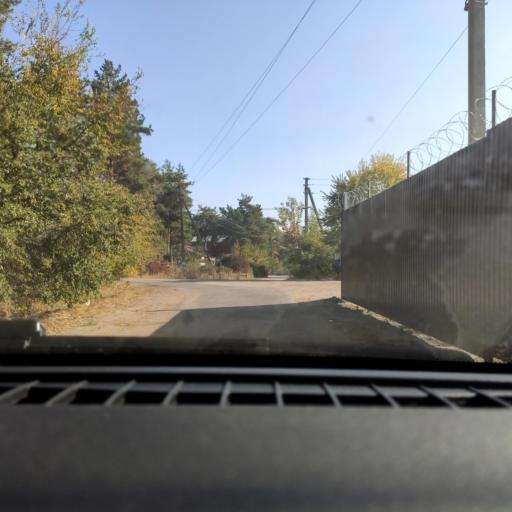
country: RU
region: Voronezj
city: Maslovka
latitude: 51.5465
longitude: 39.2209
